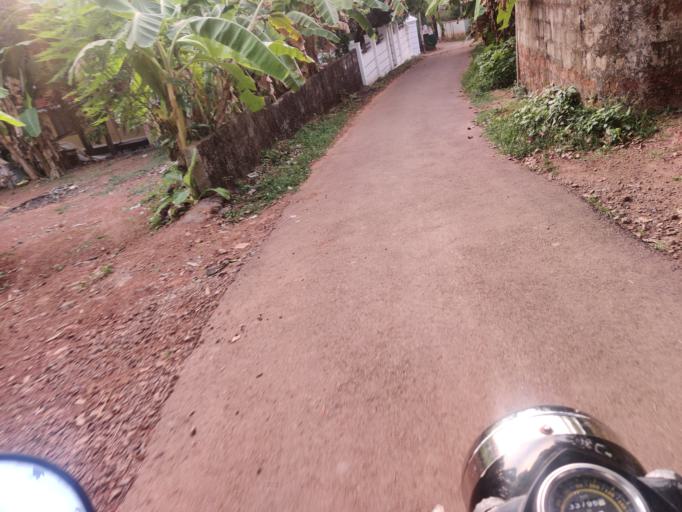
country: IN
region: Kerala
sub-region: Kozhikode
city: Mavoor
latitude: 11.2588
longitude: 75.9507
